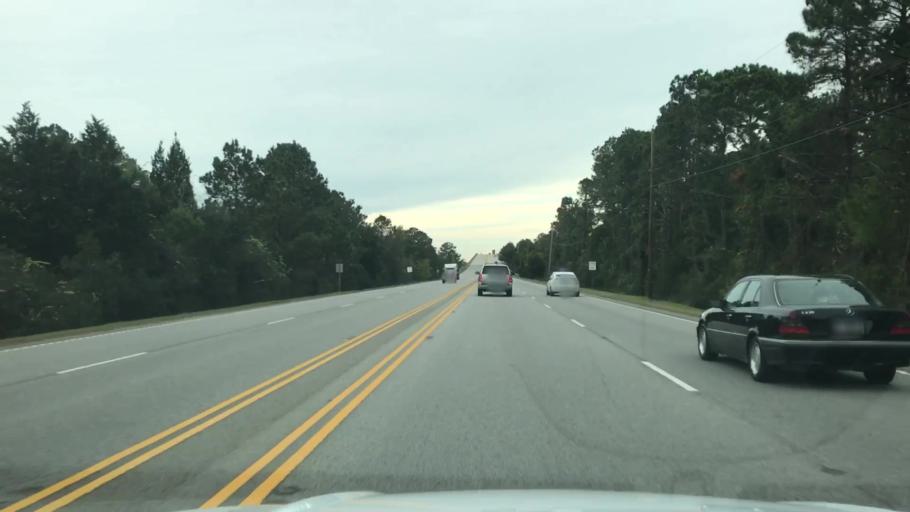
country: US
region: South Carolina
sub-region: Georgetown County
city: Georgetown
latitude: 33.3649
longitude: -79.2442
